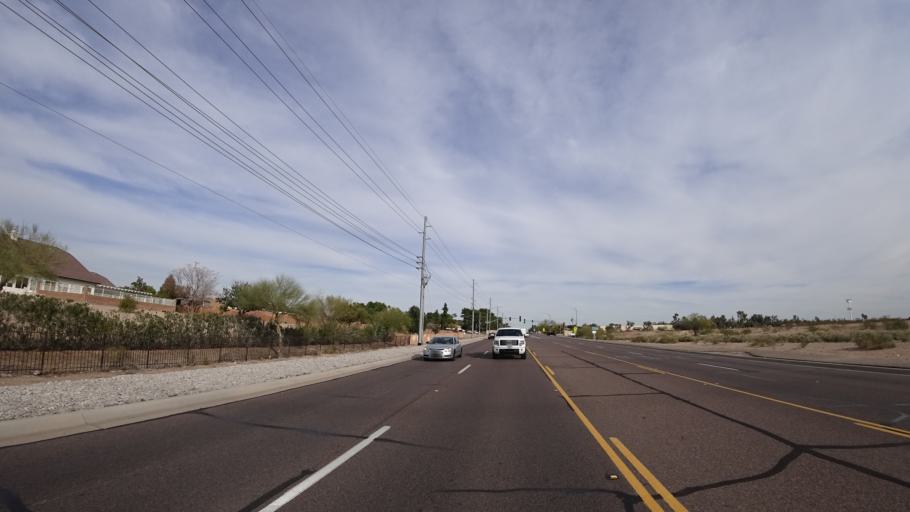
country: US
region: Arizona
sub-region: Maricopa County
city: Youngtown
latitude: 33.5655
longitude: -112.3000
